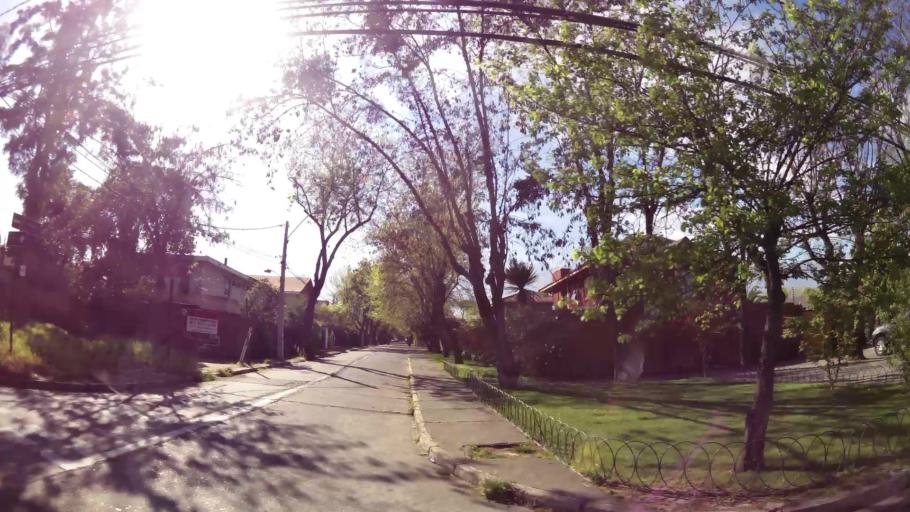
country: CL
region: Santiago Metropolitan
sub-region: Provincia de Santiago
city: Villa Presidente Frei, Nunoa, Santiago, Chile
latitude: -33.4331
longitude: -70.5575
